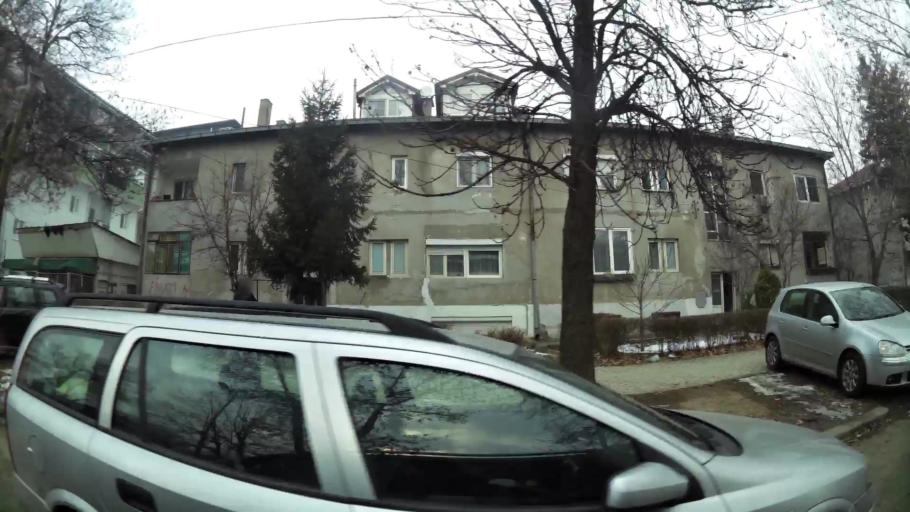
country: MK
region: Cair
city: Cair
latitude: 42.0038
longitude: 21.4647
